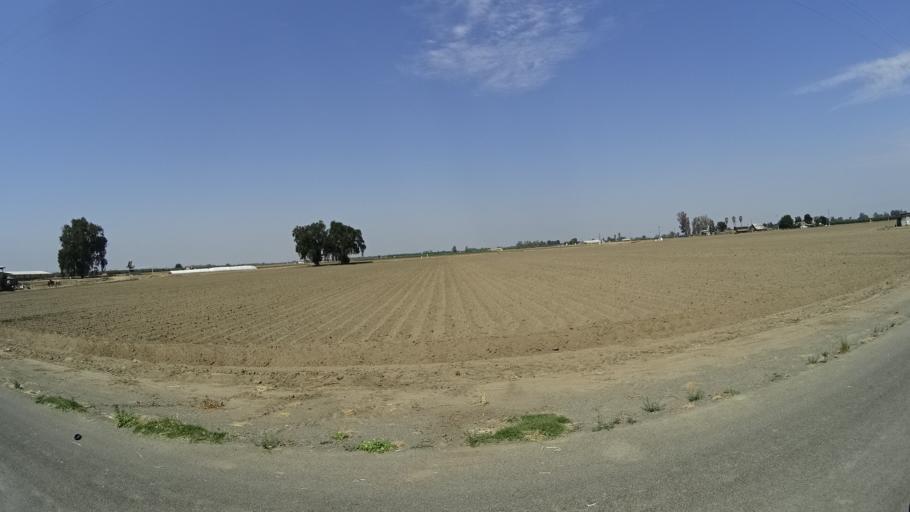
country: US
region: California
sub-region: Fresno County
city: Riverdale
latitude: 36.3995
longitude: -119.7803
